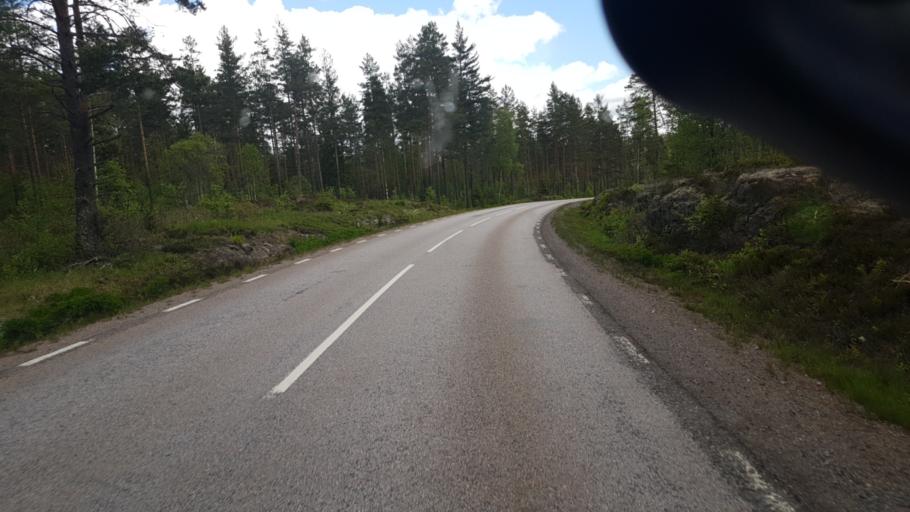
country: SE
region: Vaermland
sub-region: Arjangs Kommun
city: Arjaeng
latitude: 59.5640
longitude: 12.1842
